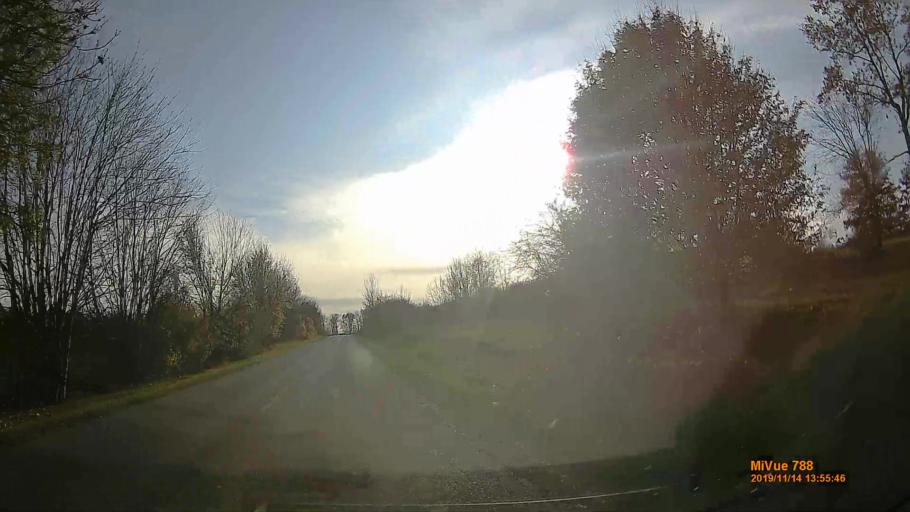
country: HU
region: Veszprem
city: Zirc
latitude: 47.2452
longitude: 17.8584
